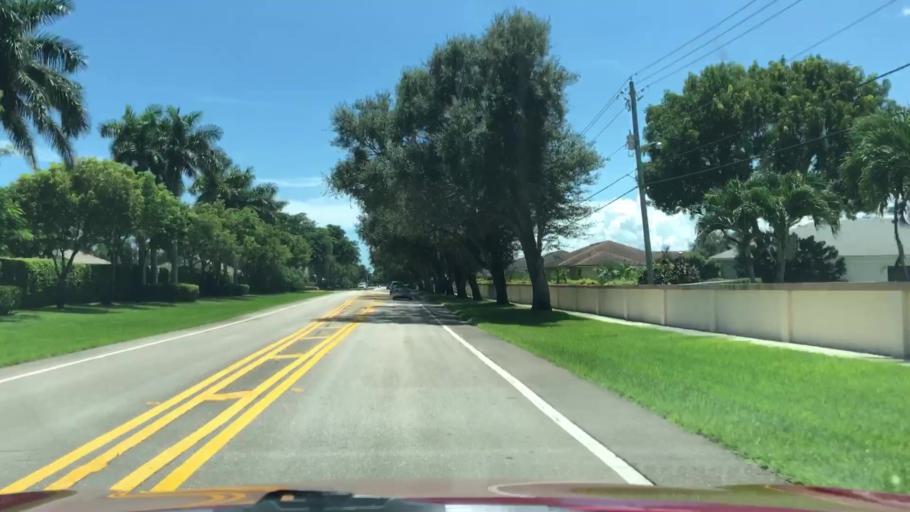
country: US
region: Florida
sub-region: Palm Beach County
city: Boynton Beach
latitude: 26.5188
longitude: -80.1066
